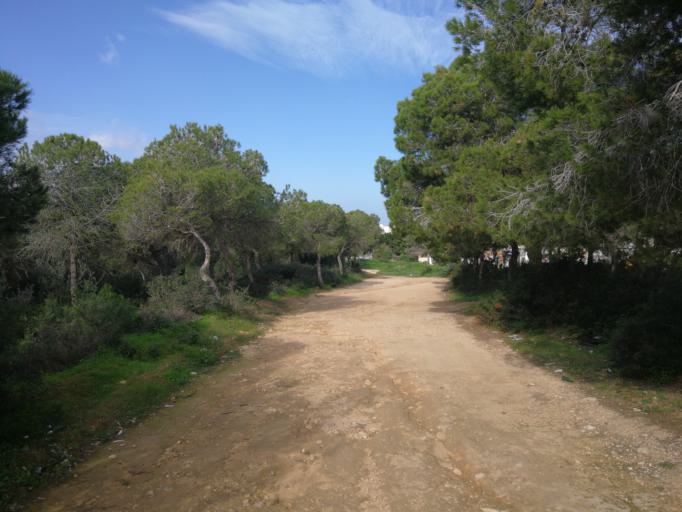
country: TN
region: Tunis
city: Al Marsa
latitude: 36.9022
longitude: 10.2964
